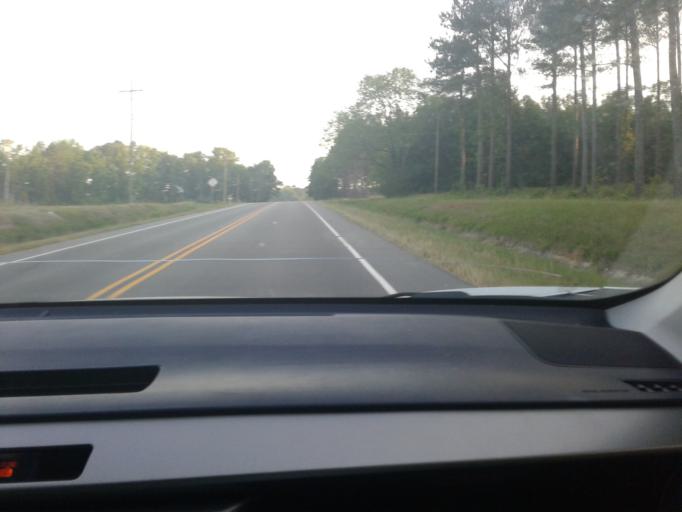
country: US
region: North Carolina
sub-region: Harnett County
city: Lillington
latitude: 35.4311
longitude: -78.8266
